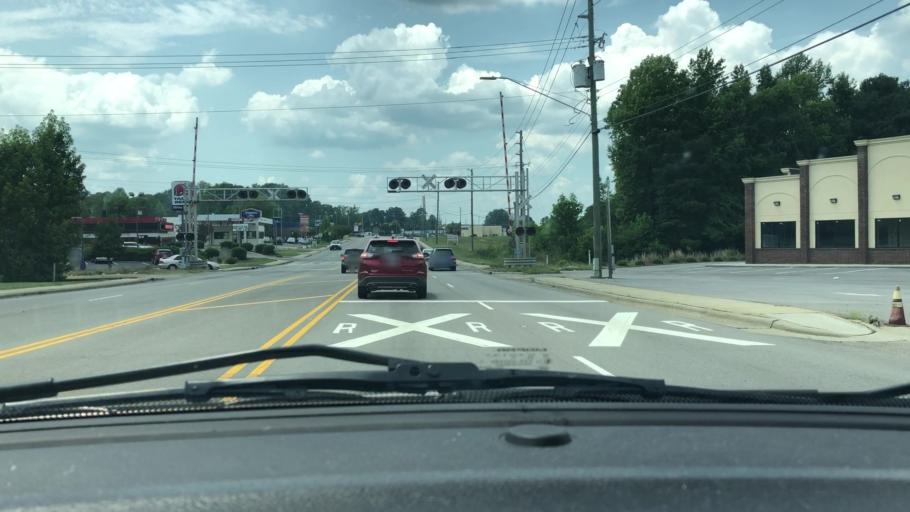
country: US
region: North Carolina
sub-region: Lee County
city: Sanford
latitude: 35.4599
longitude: -79.1569
